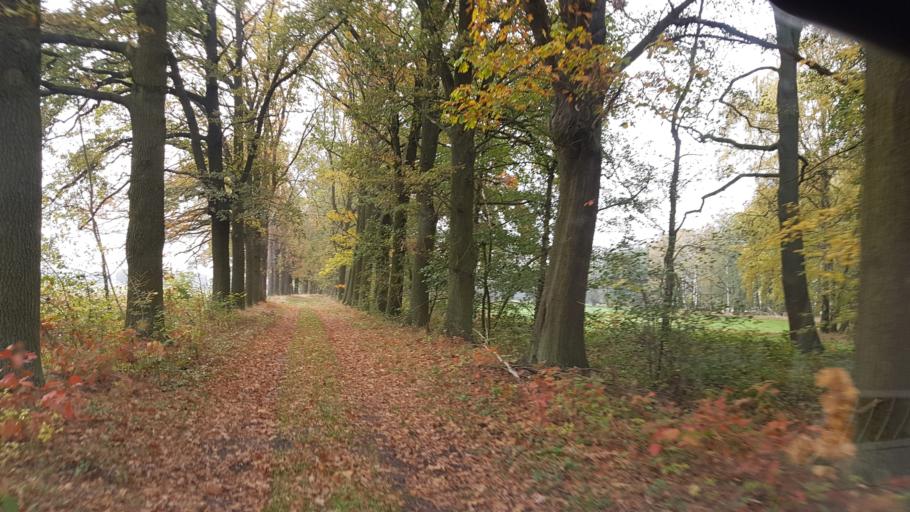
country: DE
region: Brandenburg
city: Schonewalde
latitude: 51.6941
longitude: 13.5989
